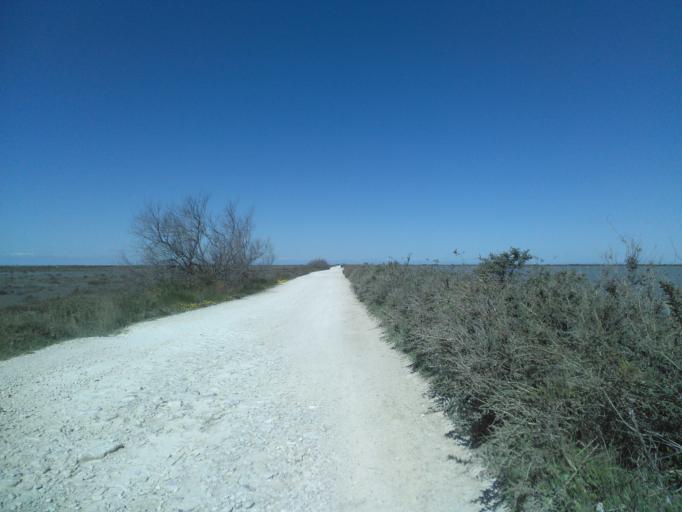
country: FR
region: Provence-Alpes-Cote d'Azur
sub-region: Departement des Bouches-du-Rhone
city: Saintes-Maries-de-la-Mer
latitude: 43.4460
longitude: 4.6036
